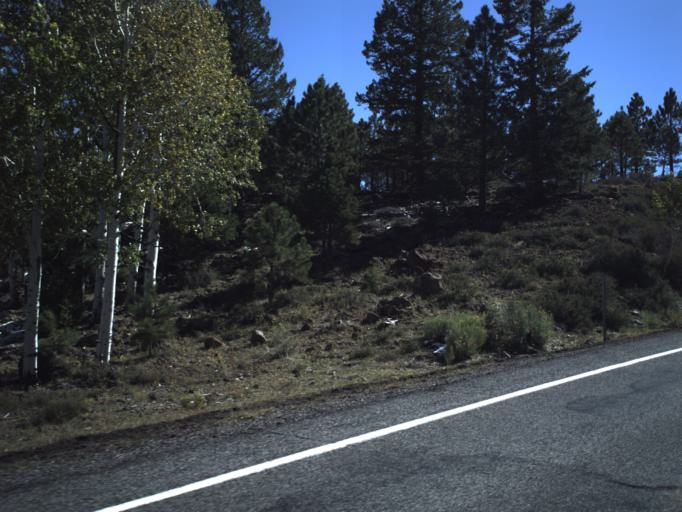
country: US
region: Utah
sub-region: Wayne County
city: Loa
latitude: 38.1574
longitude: -111.3333
